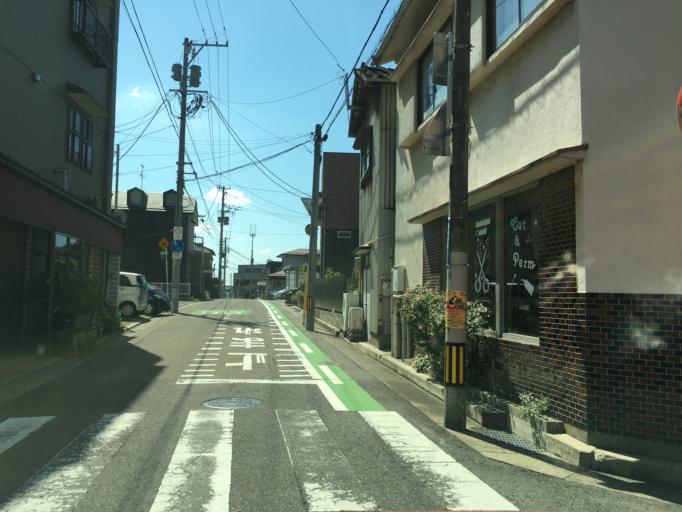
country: JP
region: Niigata
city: Niigata-shi
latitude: 37.9033
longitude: 139.0149
